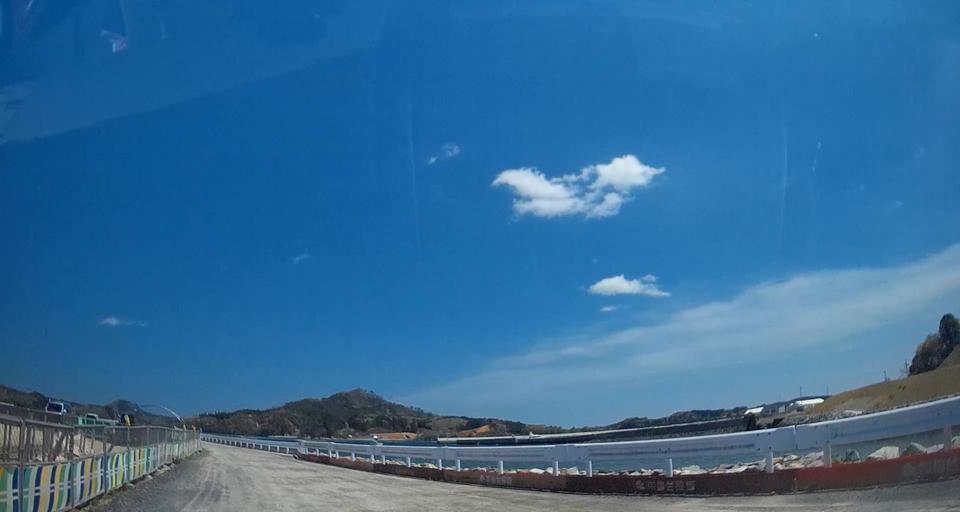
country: JP
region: Iwate
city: Ofunato
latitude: 38.8722
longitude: 141.5879
